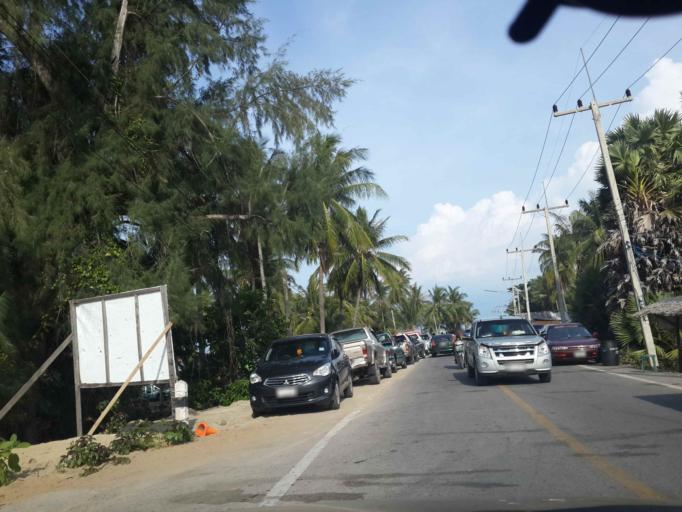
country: TH
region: Pattani
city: Yaring
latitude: 6.9291
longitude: 101.3220
